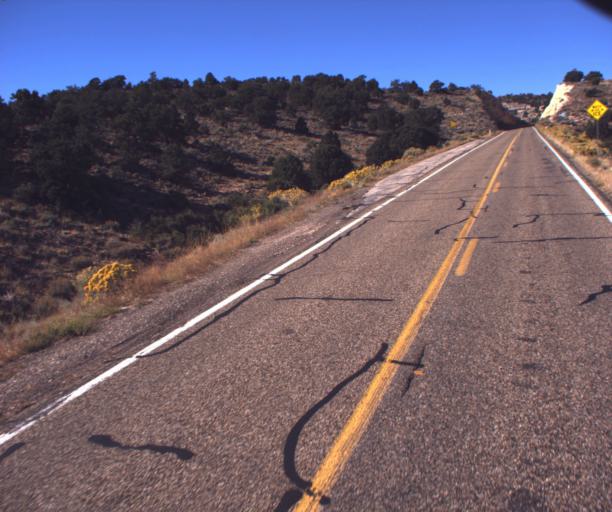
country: US
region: Arizona
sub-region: Coconino County
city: Fredonia
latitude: 36.7262
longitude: -112.0685
